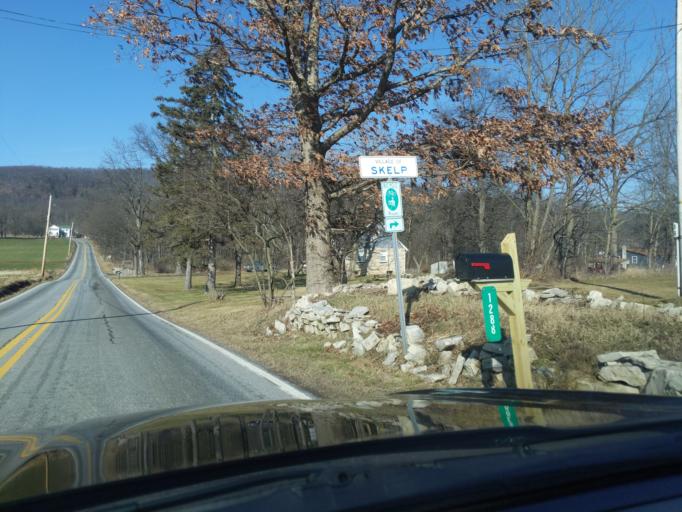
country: US
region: Pennsylvania
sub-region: Blair County
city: Tipton
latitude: 40.6164
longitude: -78.2601
